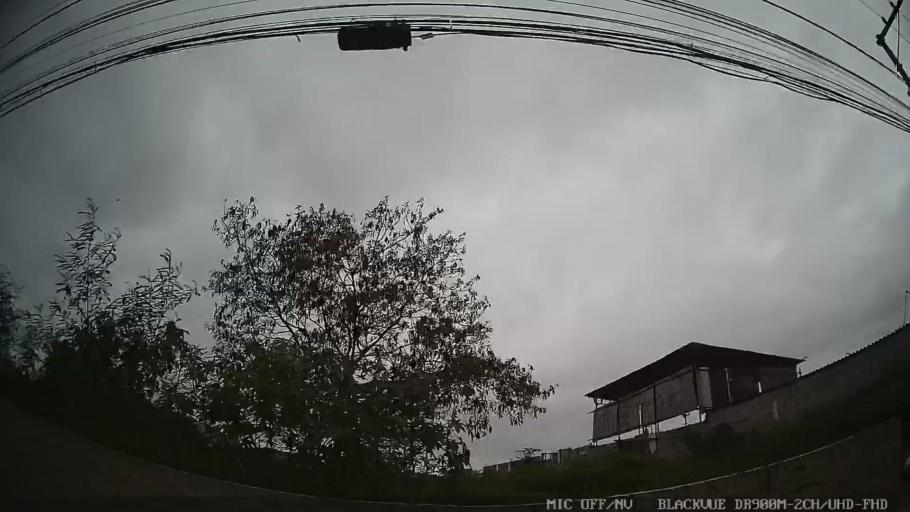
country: BR
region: Sao Paulo
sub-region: Itaquaquecetuba
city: Itaquaquecetuba
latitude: -23.4910
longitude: -46.4018
